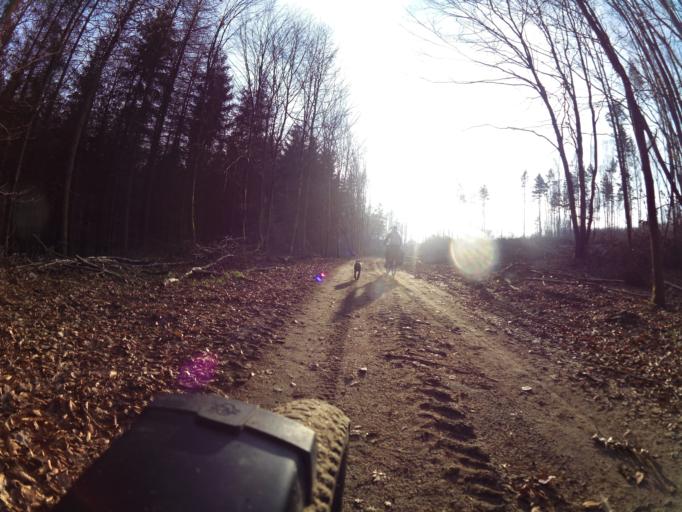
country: PL
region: West Pomeranian Voivodeship
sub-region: Powiat koszalinski
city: Polanow
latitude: 54.1643
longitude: 16.7289
